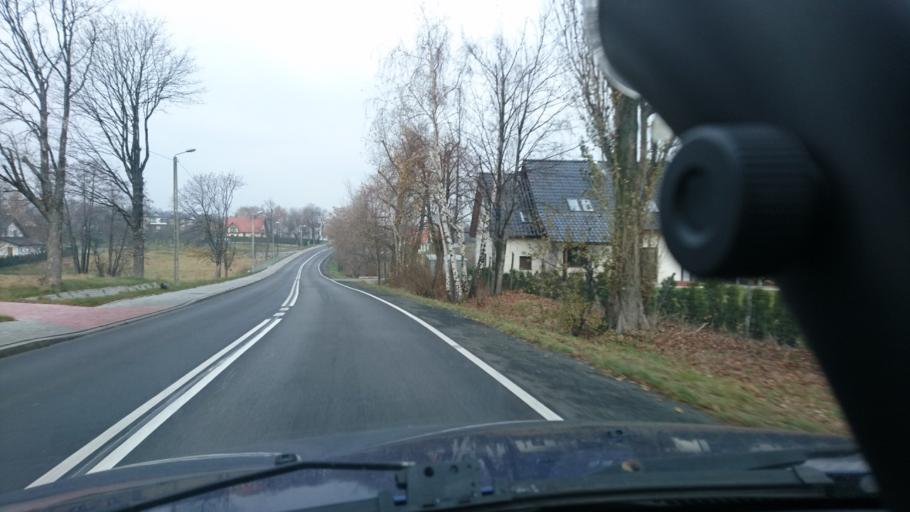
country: PL
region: Silesian Voivodeship
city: Janowice
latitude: 49.8651
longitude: 19.1168
